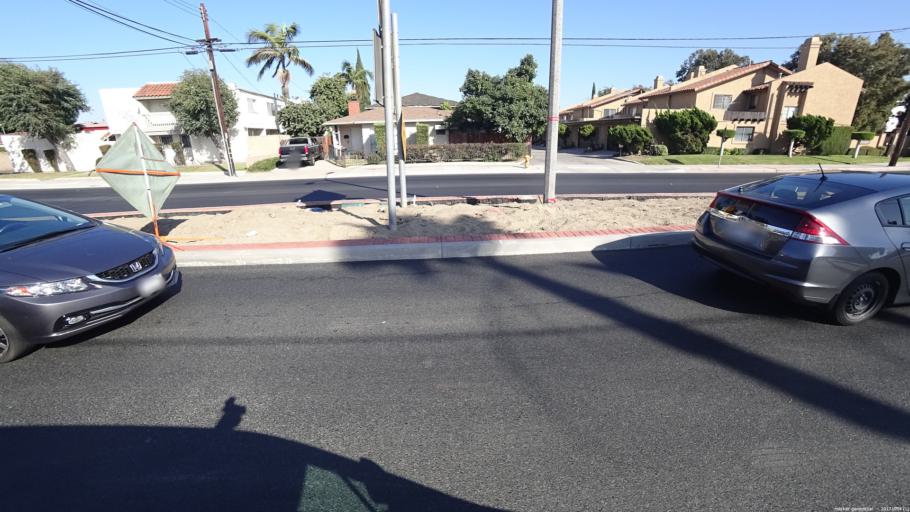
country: US
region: California
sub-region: Orange County
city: Midway City
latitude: 33.7676
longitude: -117.9725
